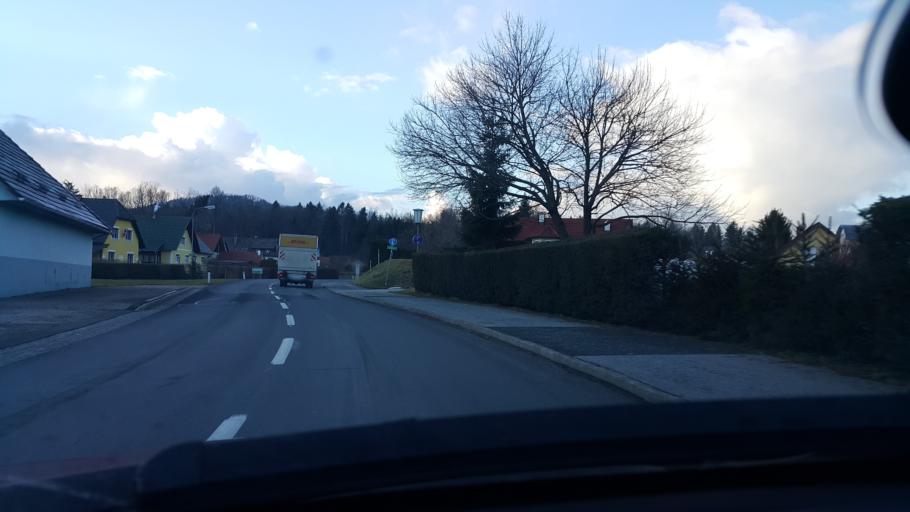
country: AT
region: Styria
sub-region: Politischer Bezirk Deutschlandsberg
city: Hollenegg
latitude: 46.7857
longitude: 15.2395
